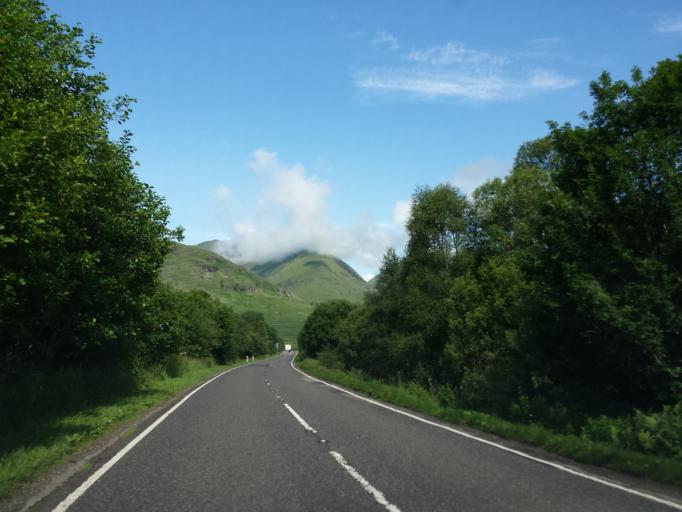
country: GB
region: Scotland
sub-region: Argyll and Bute
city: Garelochhead
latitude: 56.4067
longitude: -5.0156
